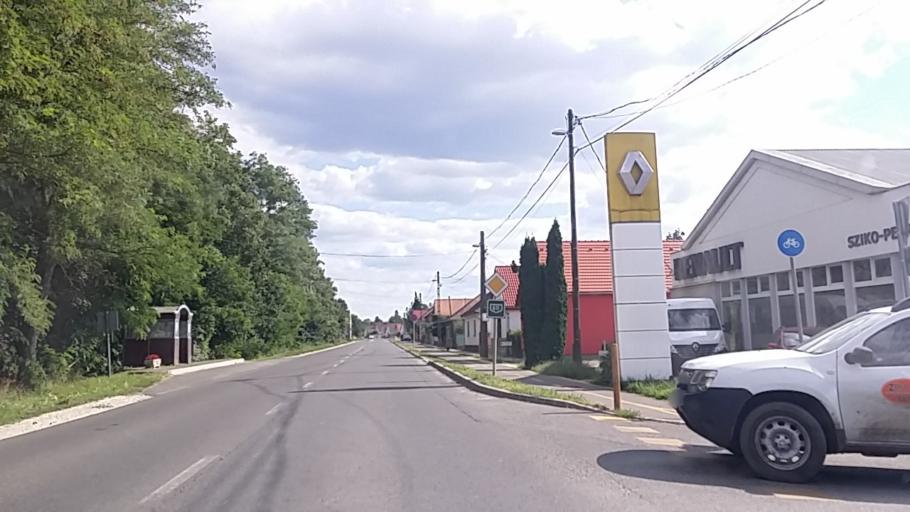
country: HU
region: Tolna
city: Dombovar
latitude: 46.3366
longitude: 18.1269
